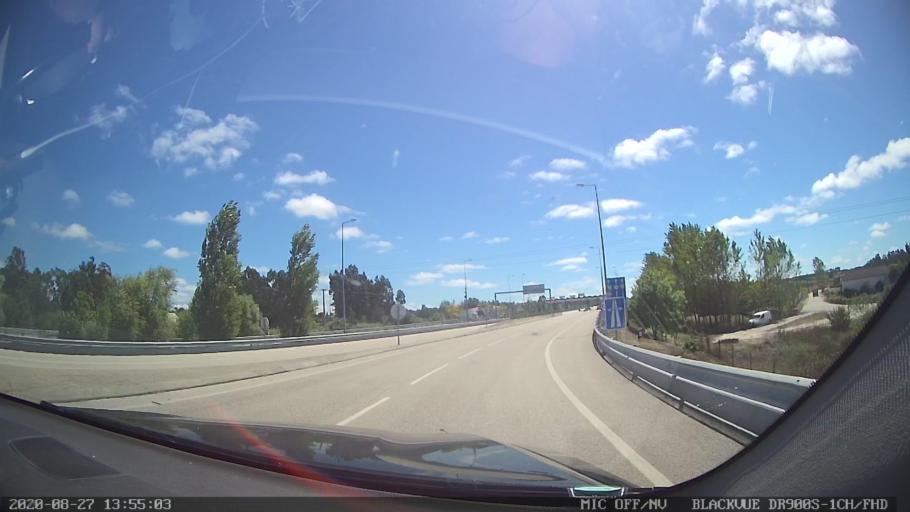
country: PT
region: Coimbra
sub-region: Montemor-O-Velho
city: Arazede
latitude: 40.3310
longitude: -8.7257
